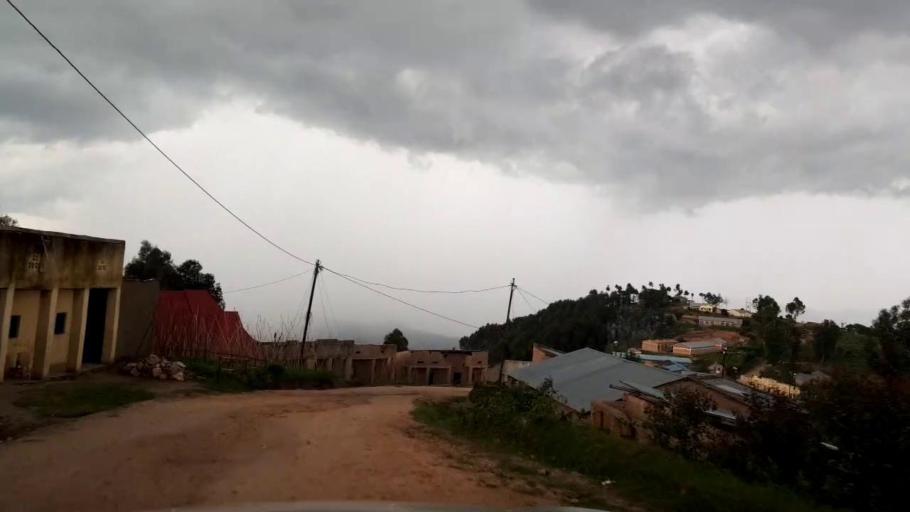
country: RW
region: Southern Province
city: Gitarama
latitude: -1.8711
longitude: 29.5897
